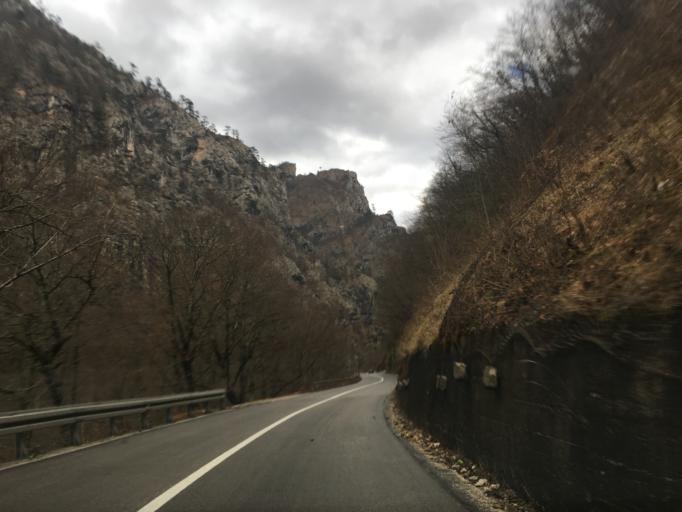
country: RS
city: Sokolovo Brdo
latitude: 43.1782
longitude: 19.7694
